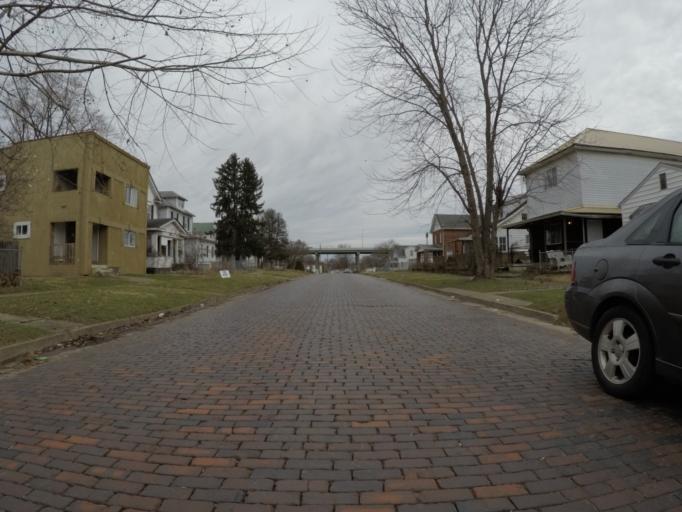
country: US
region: West Virginia
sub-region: Cabell County
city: Huntington
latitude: 38.4088
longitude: -82.4850
